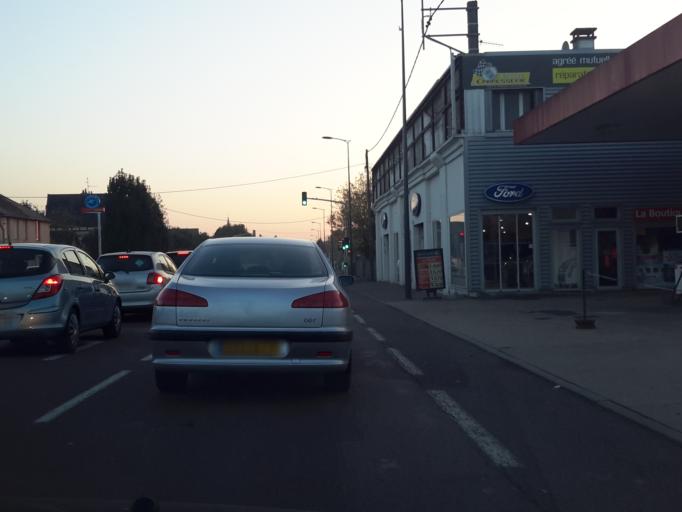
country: FR
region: Bourgogne
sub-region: Departement de la Cote-d'Or
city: Beaune
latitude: 47.0356
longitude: 4.8457
